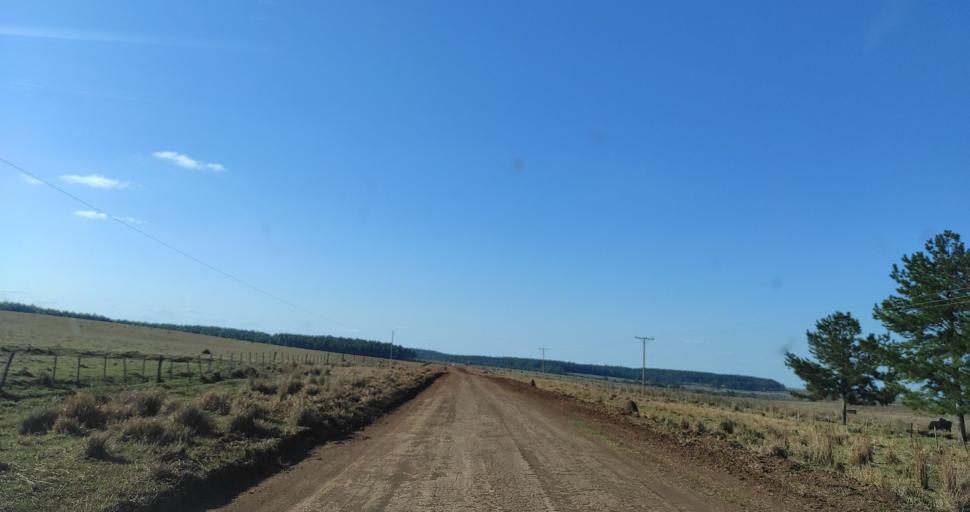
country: PY
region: Itapua
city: San Juan del Parana
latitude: -27.4325
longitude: -56.0847
